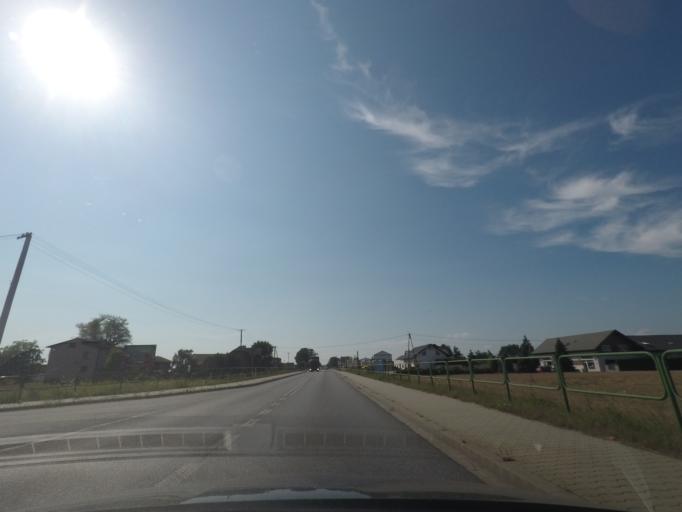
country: PL
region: Silesian Voivodeship
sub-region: Powiat pszczynski
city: Suszec
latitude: 50.0321
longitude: 18.7810
